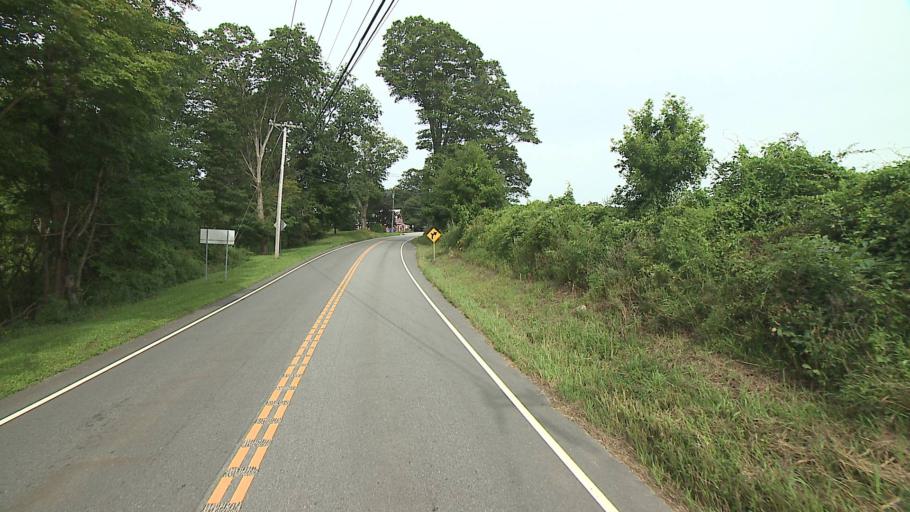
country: US
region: Connecticut
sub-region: Litchfield County
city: New Preston
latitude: 41.7200
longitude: -73.3325
